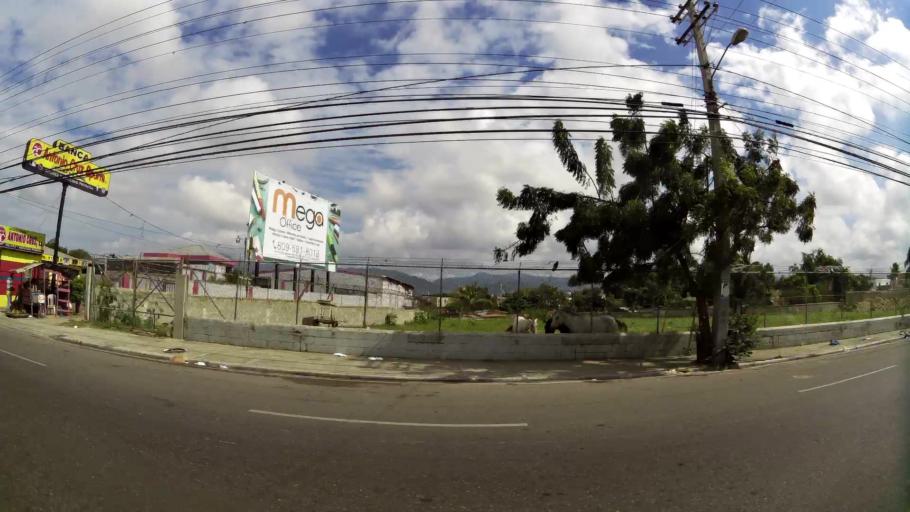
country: DO
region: Santiago
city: Santiago de los Caballeros
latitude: 19.4889
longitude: -70.7161
